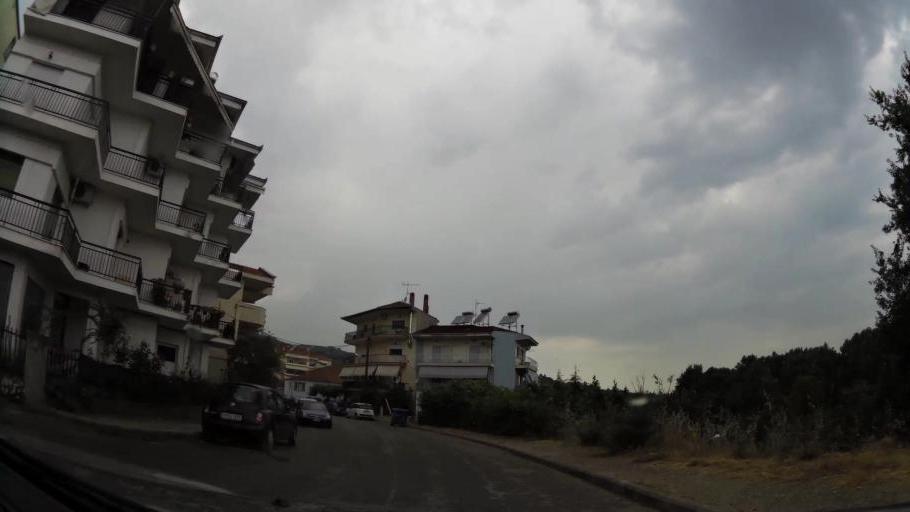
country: GR
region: Central Macedonia
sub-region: Nomos Imathias
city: Veroia
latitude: 40.5302
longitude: 22.1969
